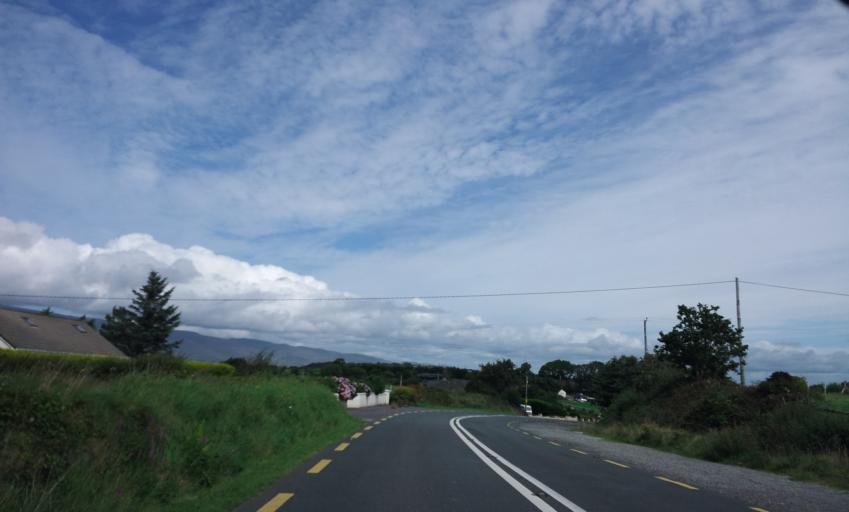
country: IE
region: Munster
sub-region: Ciarrai
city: Killorglin
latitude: 52.0919
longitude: -9.8461
